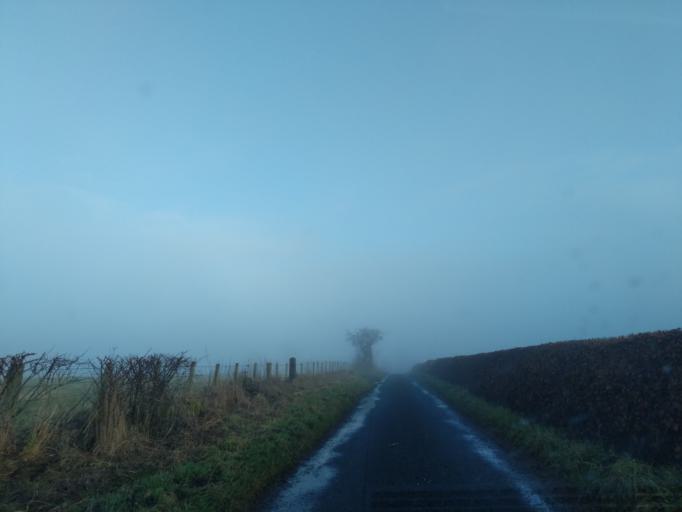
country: GB
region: Scotland
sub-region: Perth and Kinross
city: Auchterarder
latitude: 56.2842
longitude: -3.6902
